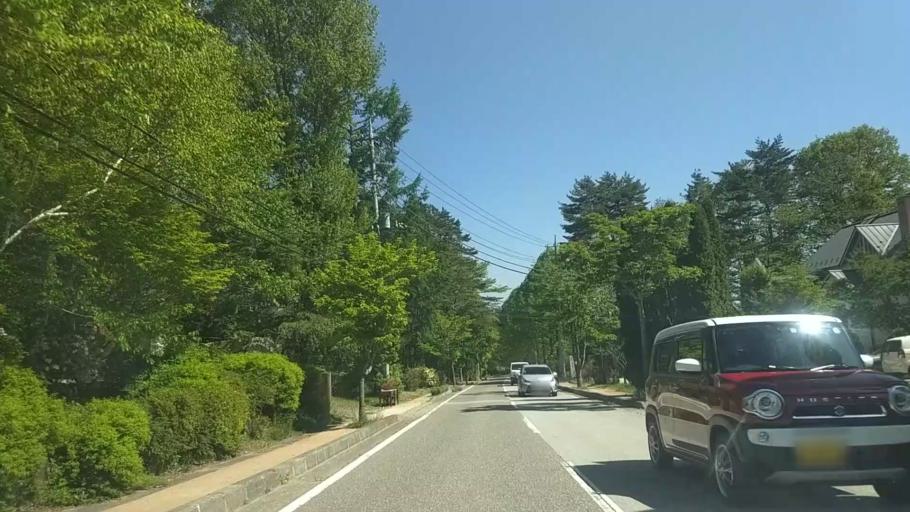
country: JP
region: Yamanashi
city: Nirasaki
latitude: 35.8966
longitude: 138.4377
